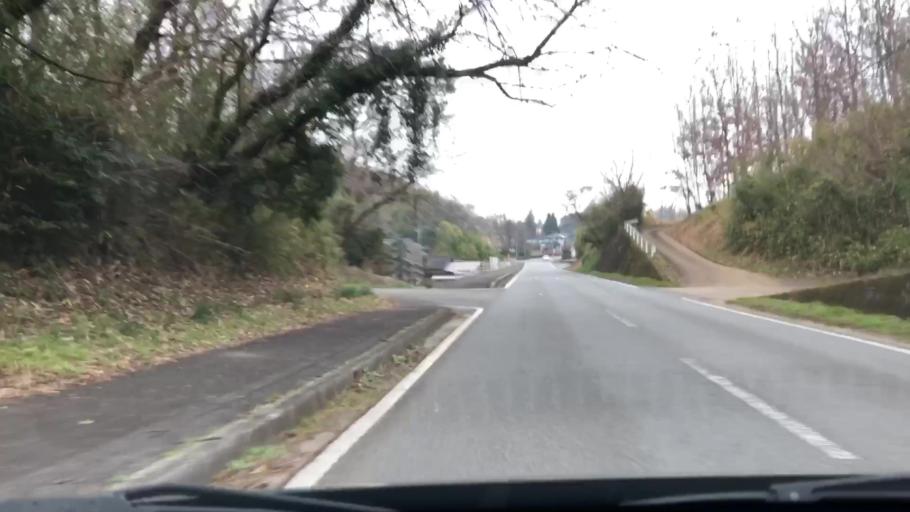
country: JP
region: Oita
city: Usuki
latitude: 33.0166
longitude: 131.6680
